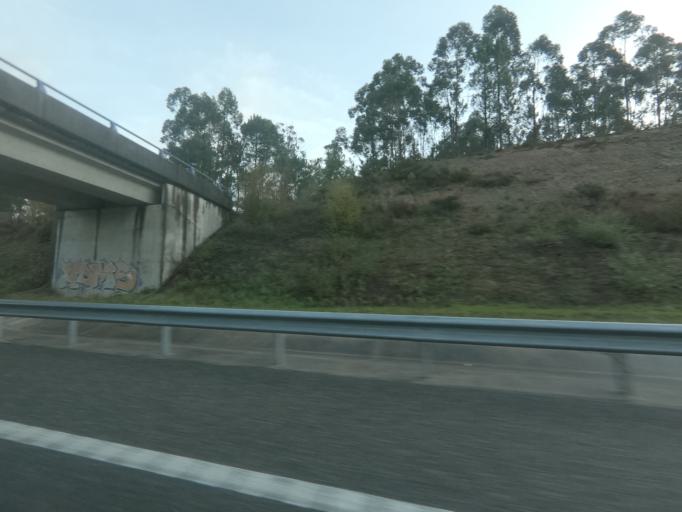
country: ES
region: Galicia
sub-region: Provincia de Pontevedra
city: Tui
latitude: 42.1029
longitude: -8.6449
